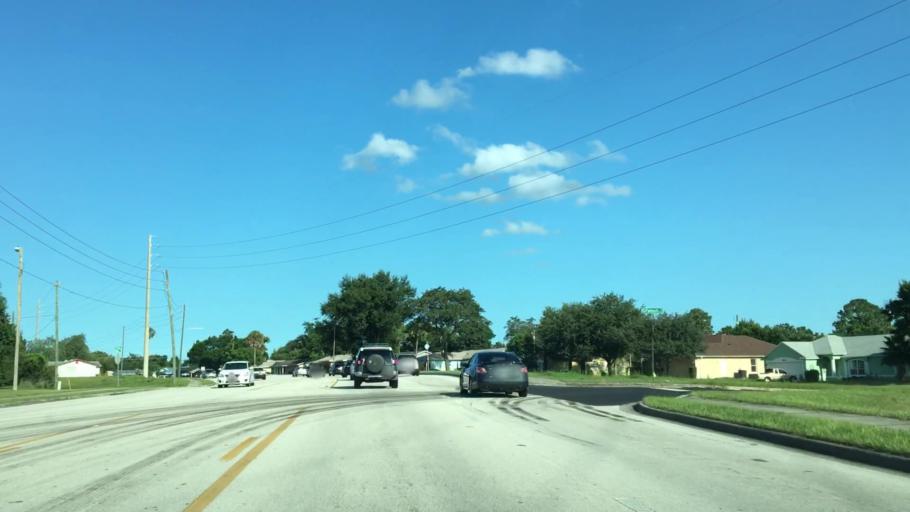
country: US
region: Florida
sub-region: Volusia County
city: Deltona
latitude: 28.9095
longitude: -81.2575
